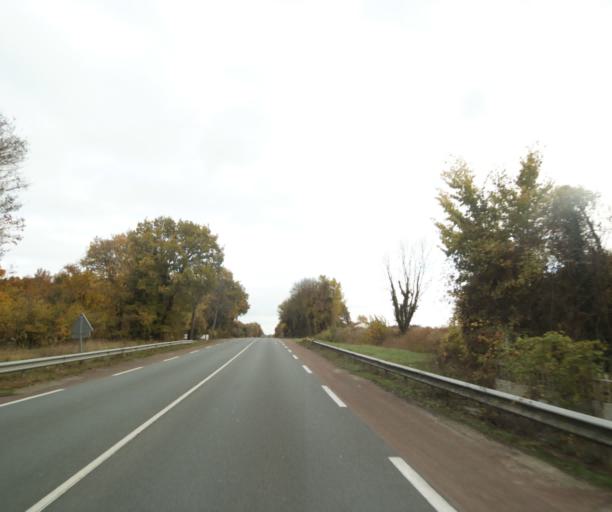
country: FR
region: Poitou-Charentes
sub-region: Departement de la Charente-Maritime
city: Saintes
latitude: 45.7626
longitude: -0.6713
